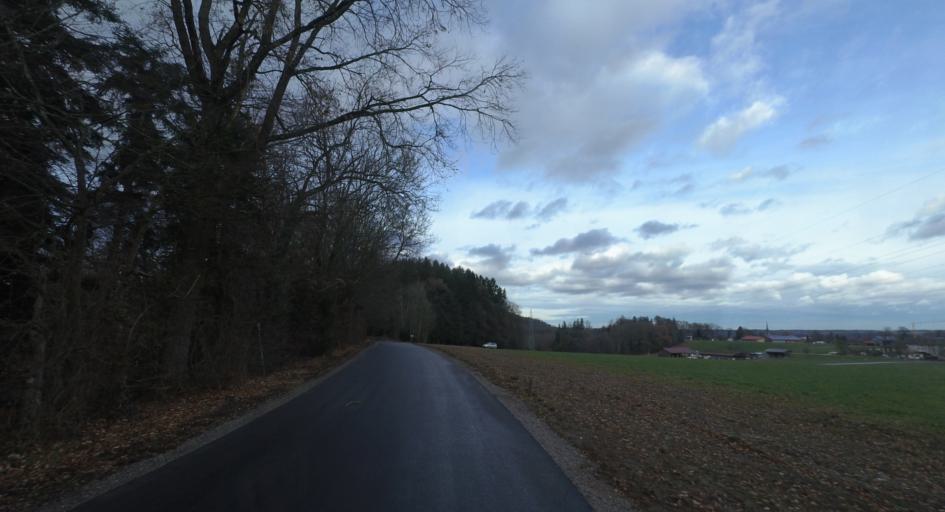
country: DE
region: Bavaria
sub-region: Upper Bavaria
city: Prien am Chiemsee
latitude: 47.8473
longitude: 12.3331
